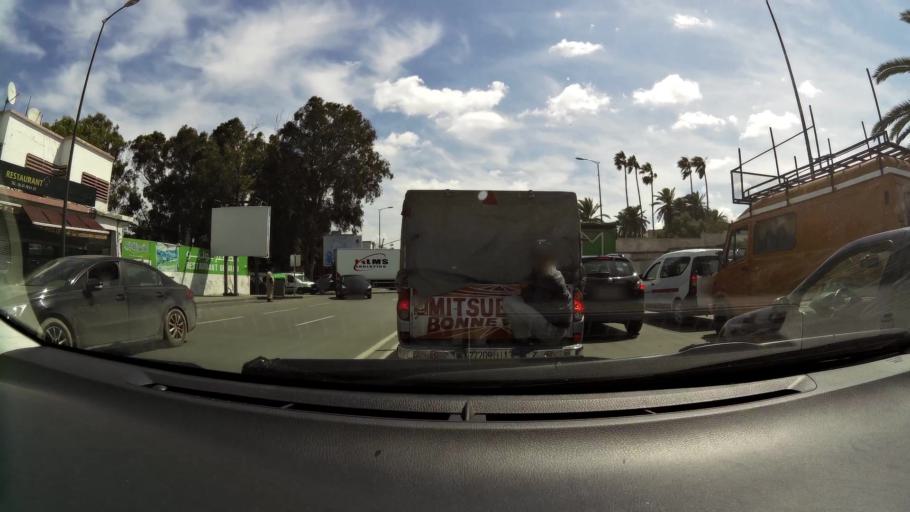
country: MA
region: Grand Casablanca
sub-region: Mediouna
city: Tit Mellil
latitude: 33.6046
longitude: -7.5375
